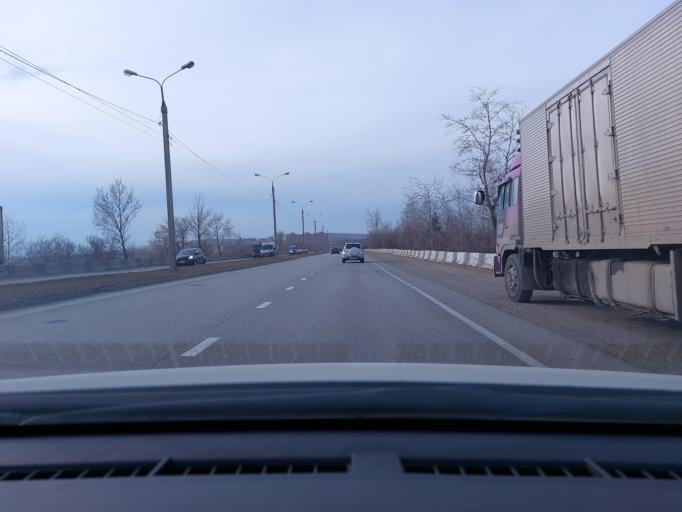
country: RU
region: Irkutsk
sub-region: Irkutskiy Rayon
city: Irkutsk
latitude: 52.3251
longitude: 104.2187
